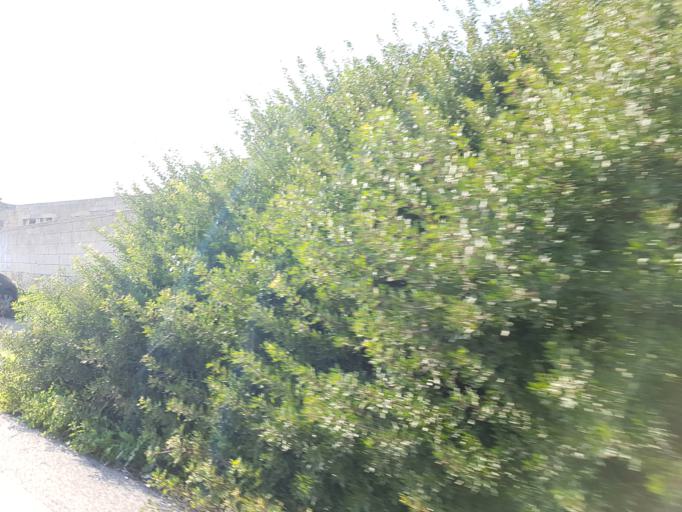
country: IT
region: Apulia
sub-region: Provincia di Brindisi
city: Materdomini
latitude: 40.6589
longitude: 17.9580
